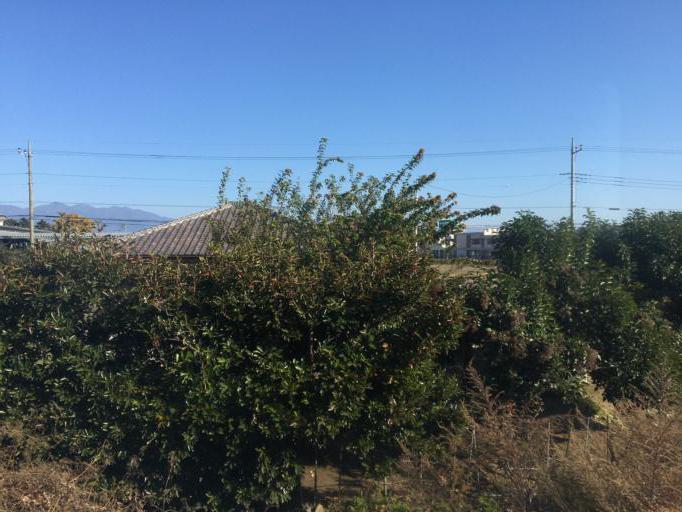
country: JP
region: Gunma
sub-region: Sawa-gun
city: Tamamura
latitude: 36.3570
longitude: 139.1341
